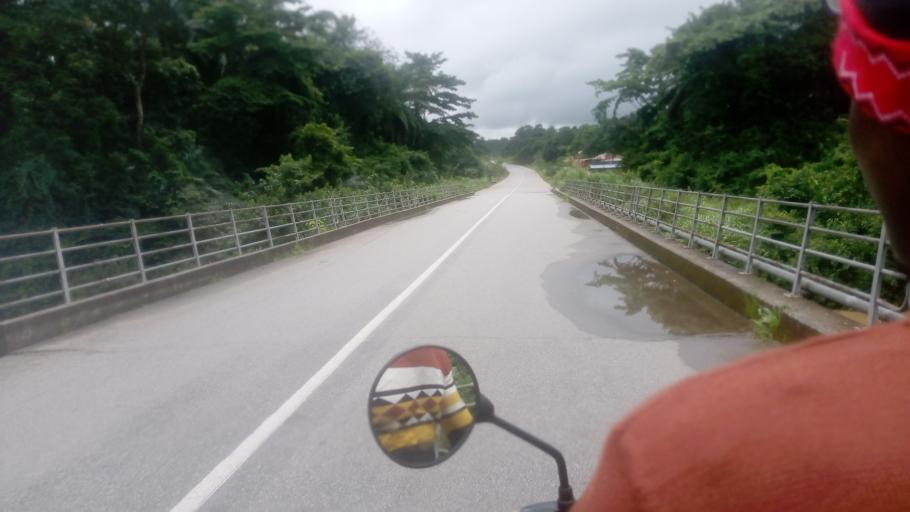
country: SL
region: Northern Province
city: Masaka
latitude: 8.6434
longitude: -11.7381
